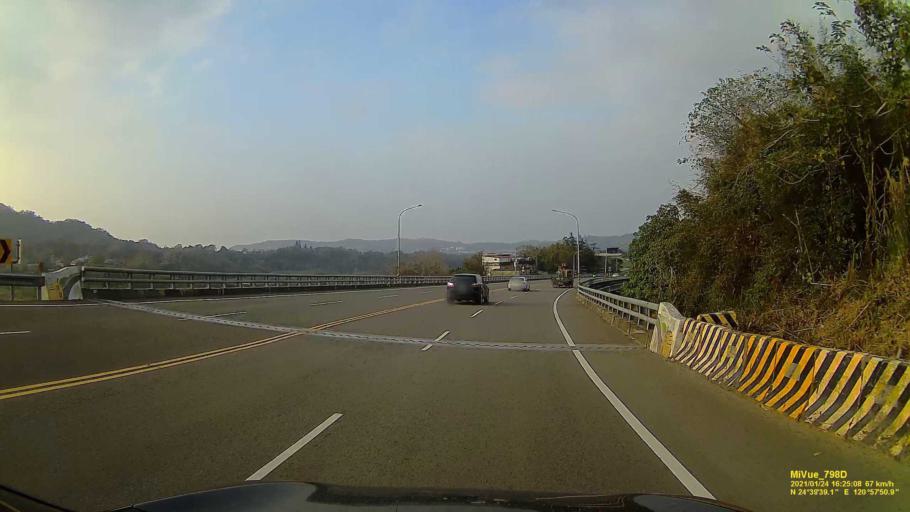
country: TW
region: Taiwan
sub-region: Hsinchu
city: Hsinchu
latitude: 24.6611
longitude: 120.9641
